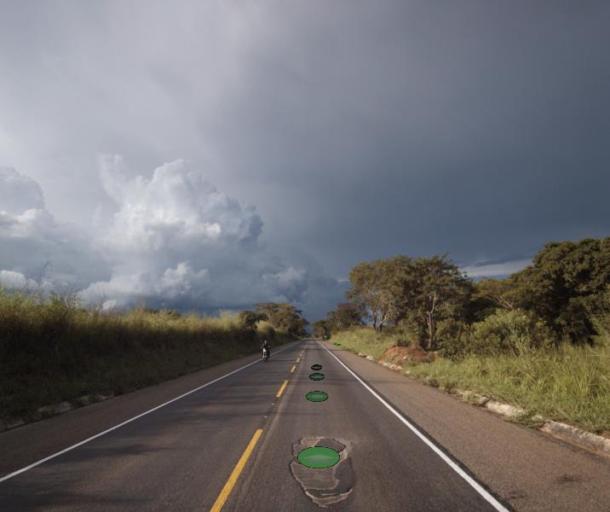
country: BR
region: Goias
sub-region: Ceres
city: Ceres
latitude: -15.1658
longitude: -49.5421
